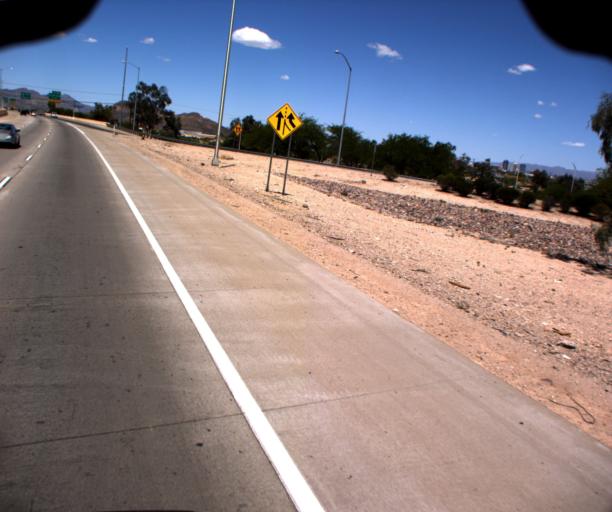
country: US
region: Arizona
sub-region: Pima County
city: South Tucson
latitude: 32.1831
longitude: -110.9545
